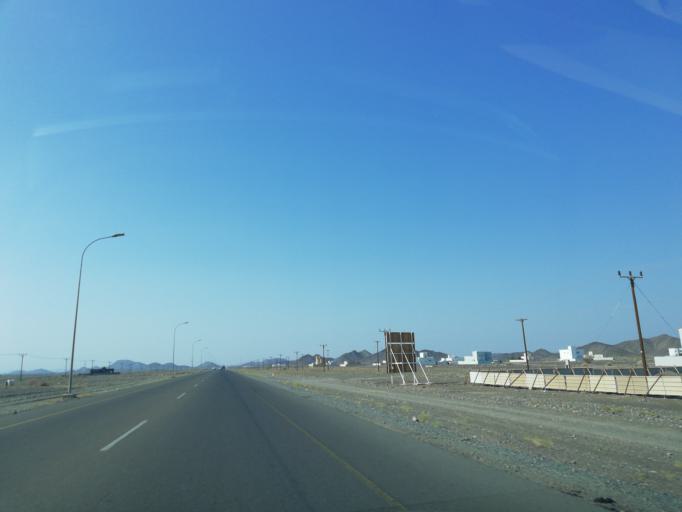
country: OM
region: Ash Sharqiyah
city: Ibra'
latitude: 22.7665
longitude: 58.1448
